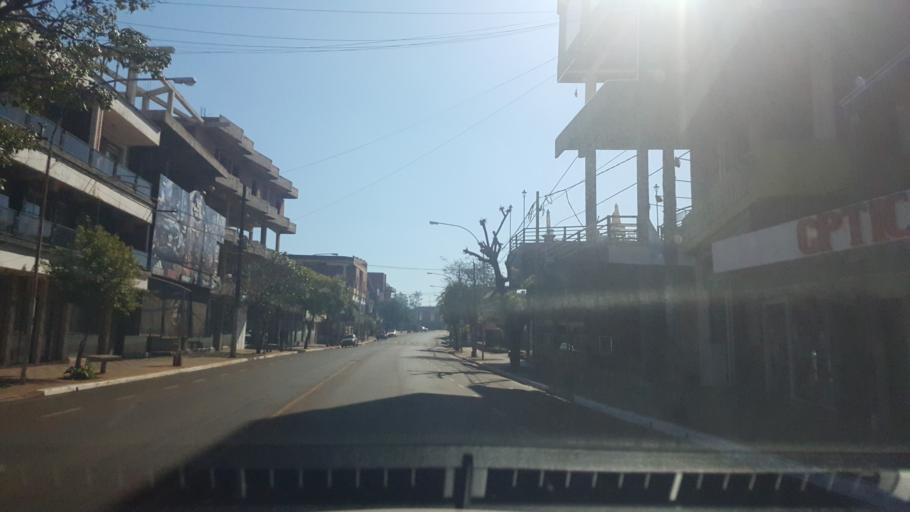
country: AR
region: Misiones
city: Puerto Rico
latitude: -26.8108
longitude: -55.0257
